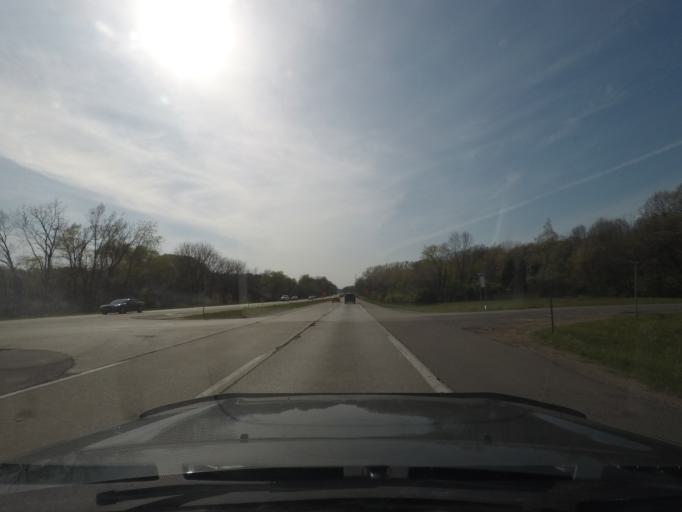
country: US
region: Michigan
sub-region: Berrien County
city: Niles
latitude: 41.8023
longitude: -86.2834
